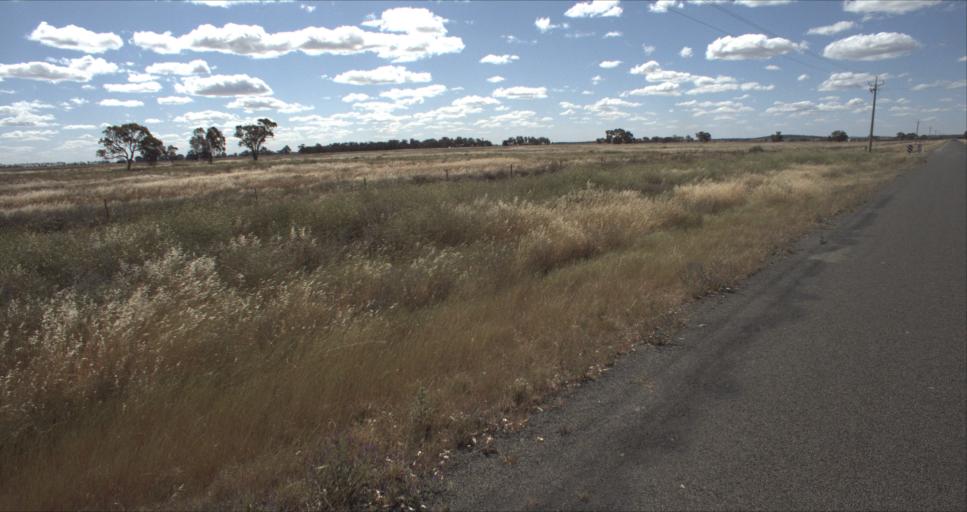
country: AU
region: New South Wales
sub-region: Leeton
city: Leeton
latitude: -34.4721
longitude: 146.2507
